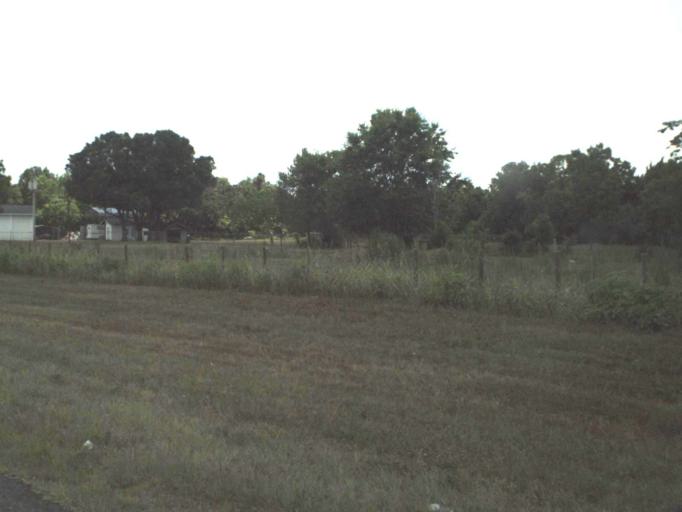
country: US
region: Florida
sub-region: Marion County
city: Ocala
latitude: 29.2378
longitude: -82.1519
